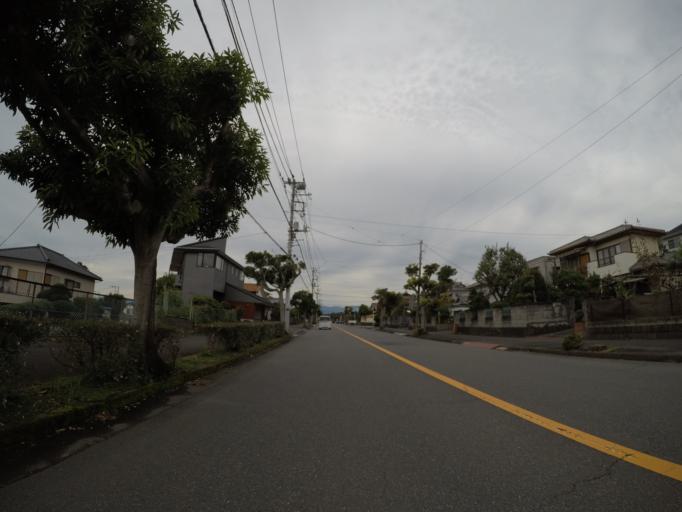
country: JP
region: Shizuoka
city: Fuji
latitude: 35.1808
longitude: 138.7112
